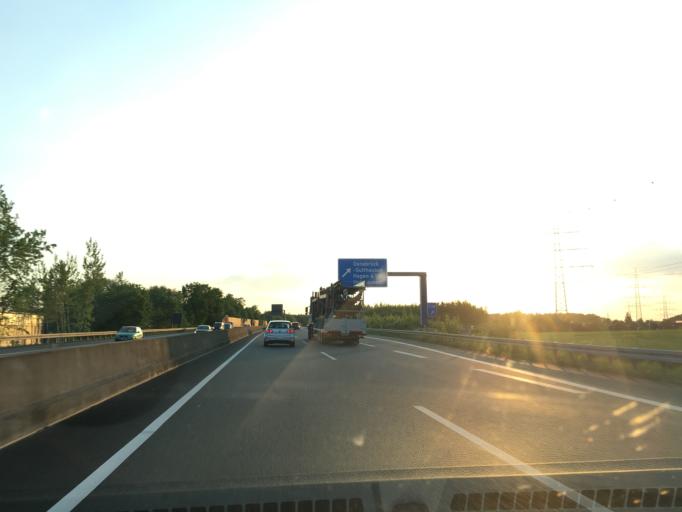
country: DE
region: Lower Saxony
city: Osnabrueck
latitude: 52.2442
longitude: 8.0430
